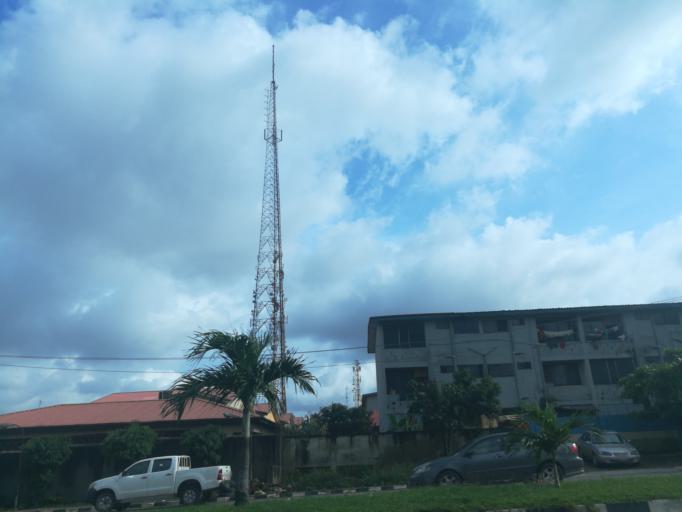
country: NG
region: Lagos
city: Ikeja
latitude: 6.6211
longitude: 3.3616
